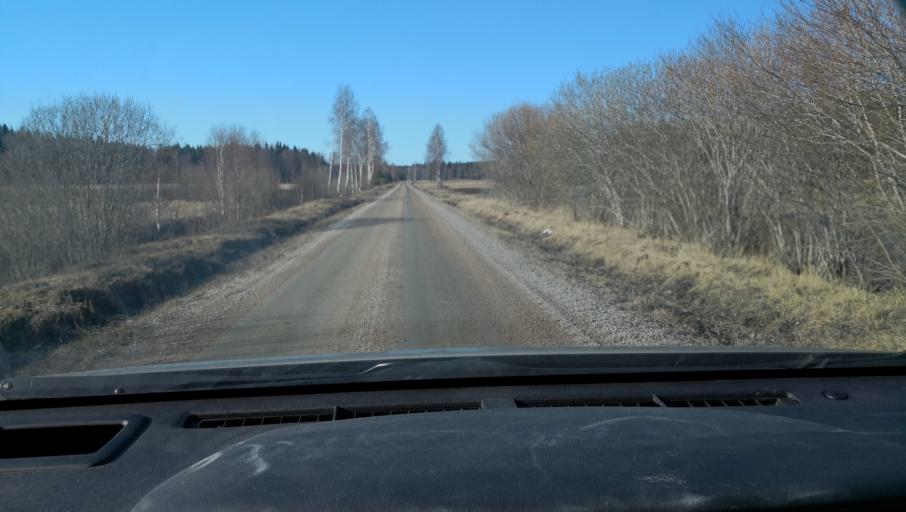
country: SE
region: Vaestmanland
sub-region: Sala Kommun
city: Sala
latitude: 60.1248
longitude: 16.6563
